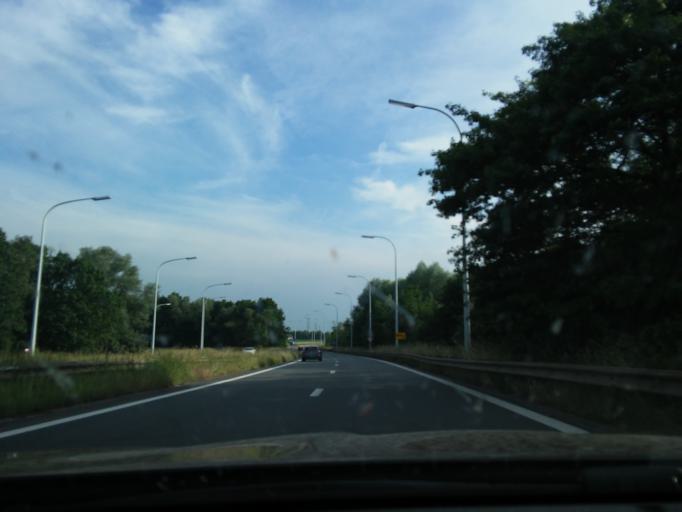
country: BE
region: Flanders
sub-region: Provincie Antwerpen
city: Kontich
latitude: 51.1271
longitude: 4.4268
